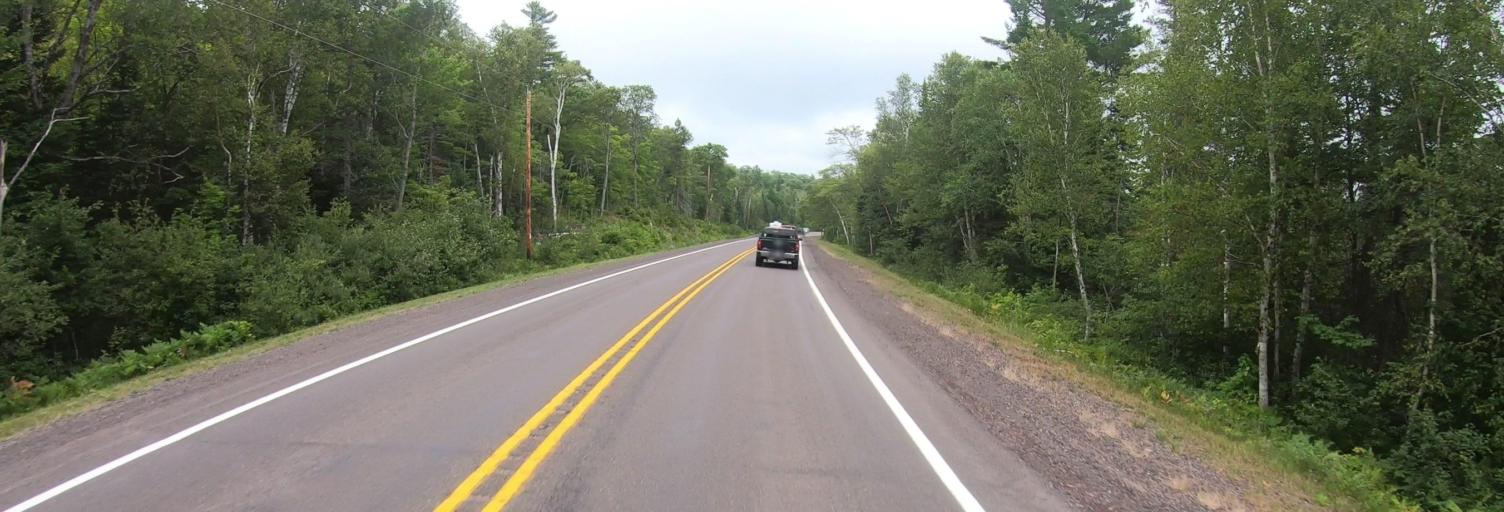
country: US
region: Michigan
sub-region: Keweenaw County
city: Eagle River
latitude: 47.4176
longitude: -88.1538
